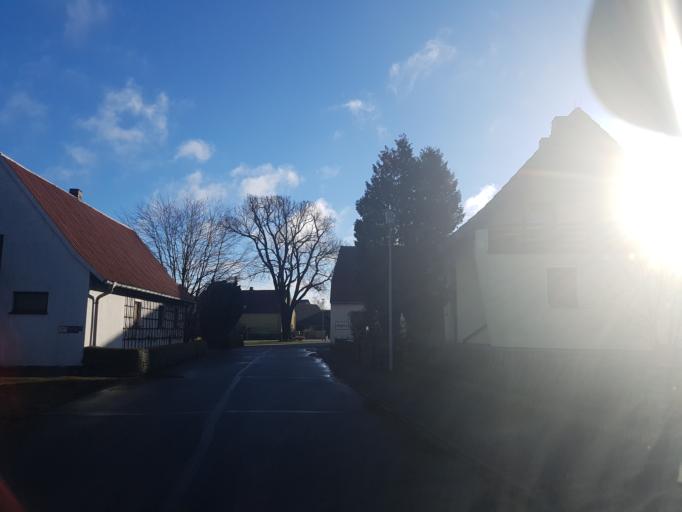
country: DE
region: Brandenburg
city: Bad Liebenwerda
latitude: 51.4938
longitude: 13.3319
